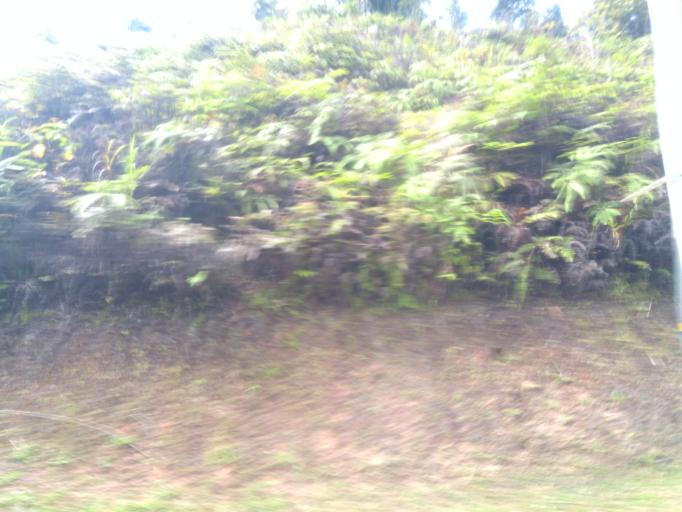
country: MY
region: Pahang
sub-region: Cameron Highlands
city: Tanah Rata
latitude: 4.4672
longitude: 101.3666
